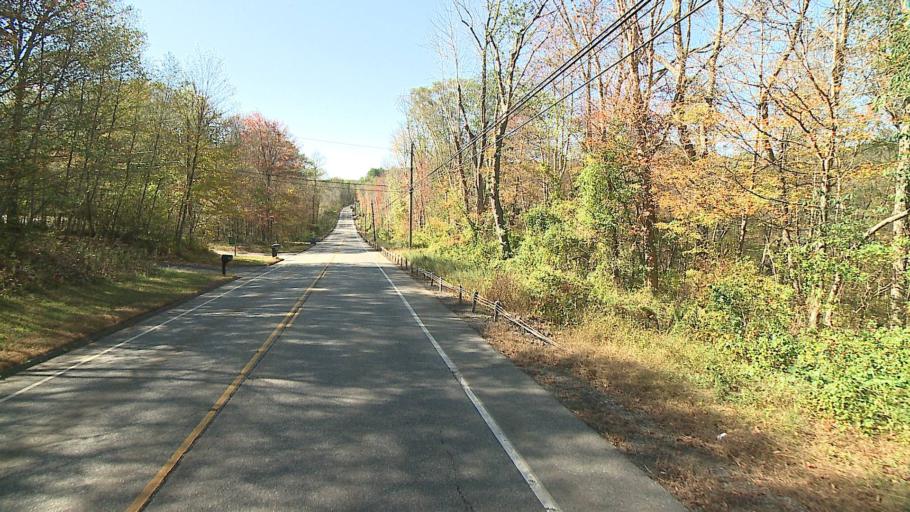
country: US
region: Connecticut
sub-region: Tolland County
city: Hebron
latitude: 41.6499
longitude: -72.3976
